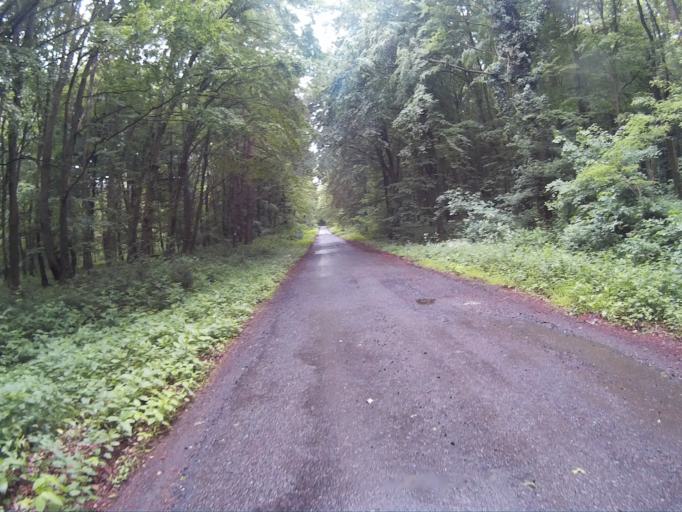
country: HU
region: Veszprem
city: Sumeg
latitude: 46.9380
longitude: 17.2909
